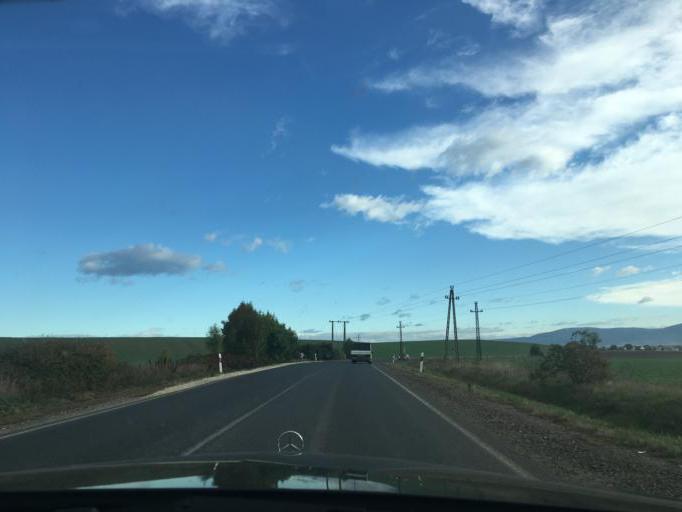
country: HU
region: Borsod-Abauj-Zemplen
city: Encs
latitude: 48.3542
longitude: 21.1277
